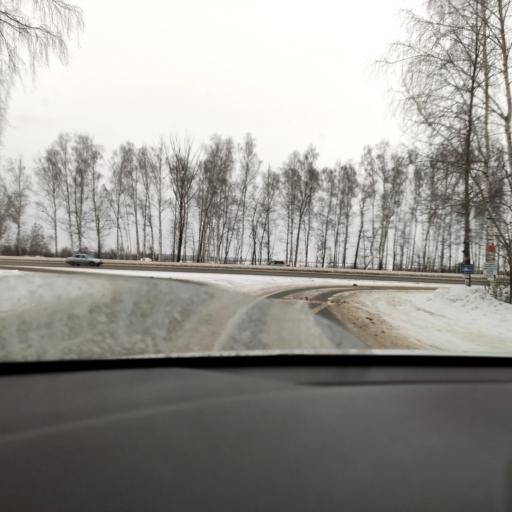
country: RU
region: Tatarstan
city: Osinovo
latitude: 55.8612
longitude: 48.8204
